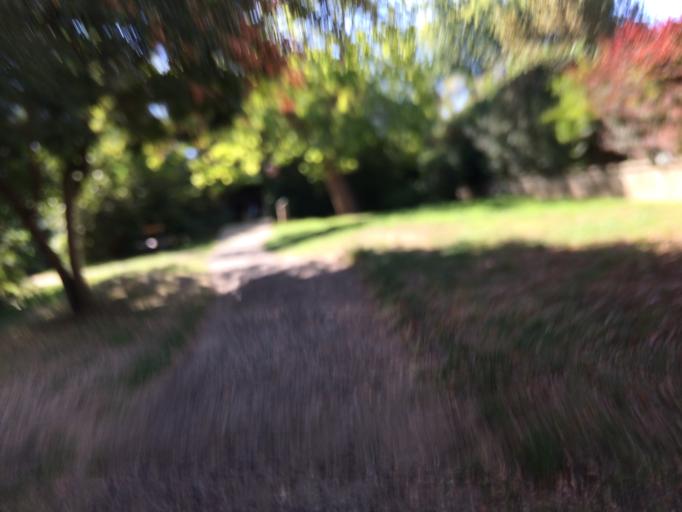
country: FR
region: Ile-de-France
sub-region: Departement de l'Essonne
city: Orsay
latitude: 48.7026
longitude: 2.2027
